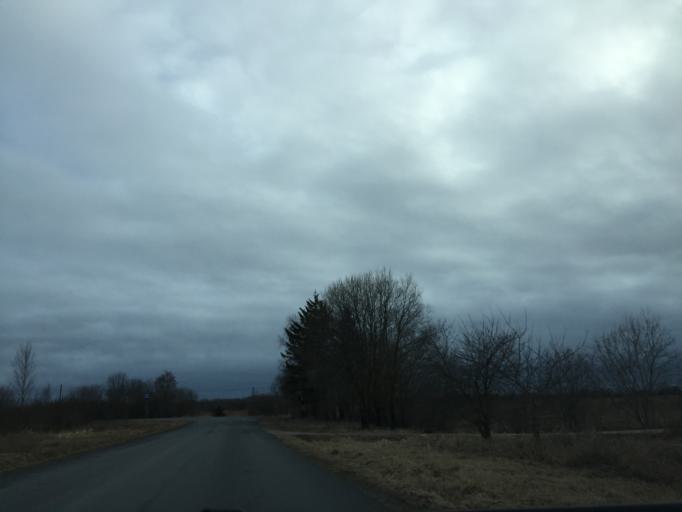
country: EE
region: Laeaene
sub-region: Haapsalu linn
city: Haapsalu
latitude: 58.8096
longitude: 23.5475
